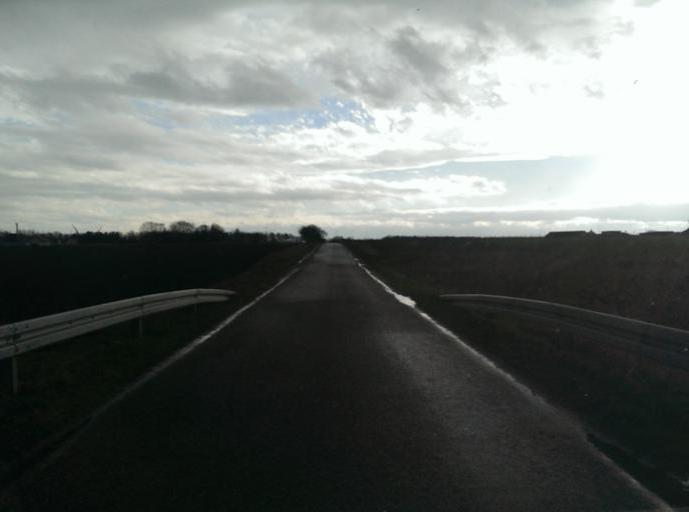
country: DK
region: South Denmark
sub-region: Esbjerg Kommune
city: Tjaereborg
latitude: 55.4687
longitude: 8.5917
